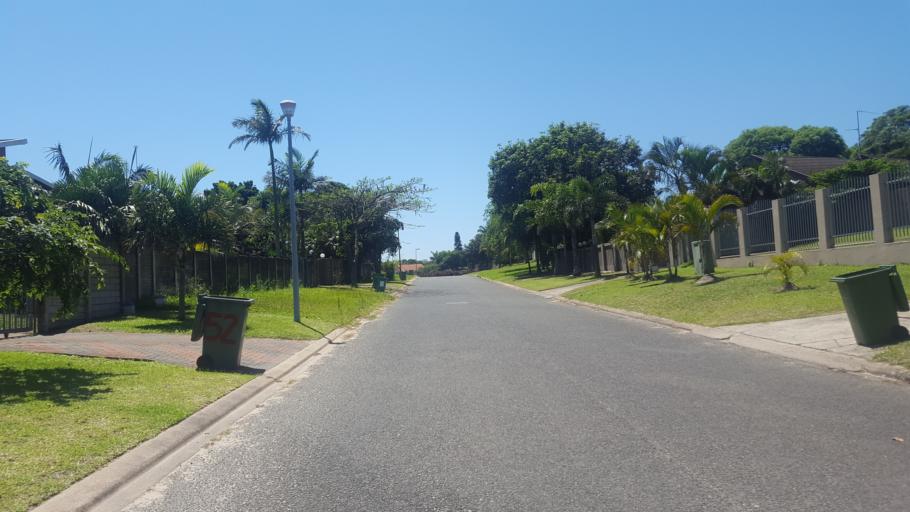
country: ZA
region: KwaZulu-Natal
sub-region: uThungulu District Municipality
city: Richards Bay
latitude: -28.7647
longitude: 32.0633
